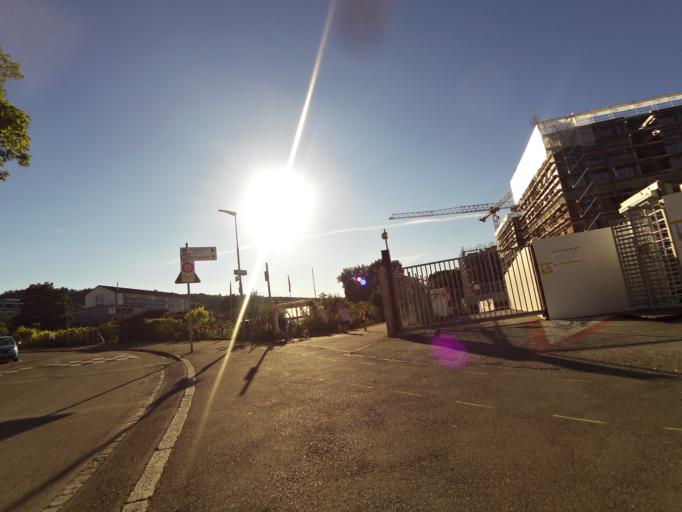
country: CH
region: Zurich
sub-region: Bezirk Zuerich
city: Zuerich (Kreis 9) / Albisrieden
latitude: 47.3788
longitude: 8.4892
